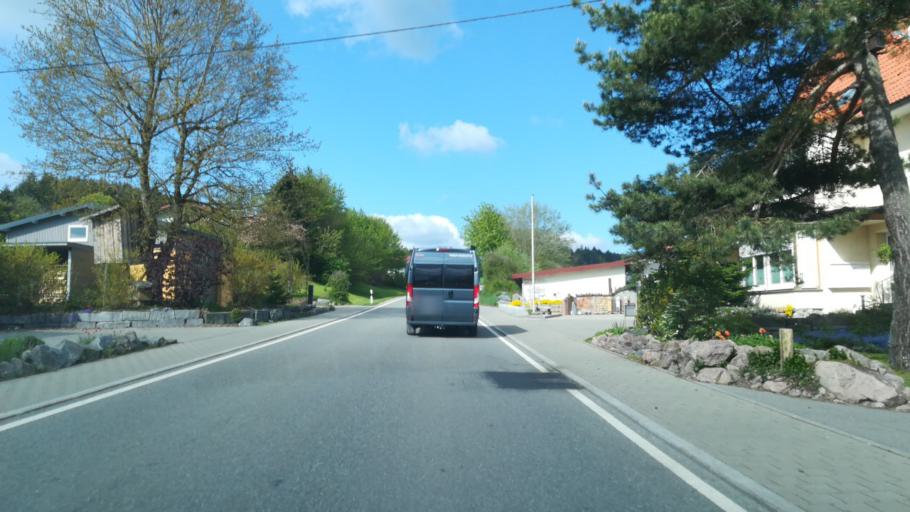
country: DE
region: Baden-Wuerttemberg
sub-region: Freiburg Region
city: Tengen
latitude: 47.8155
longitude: 8.6085
